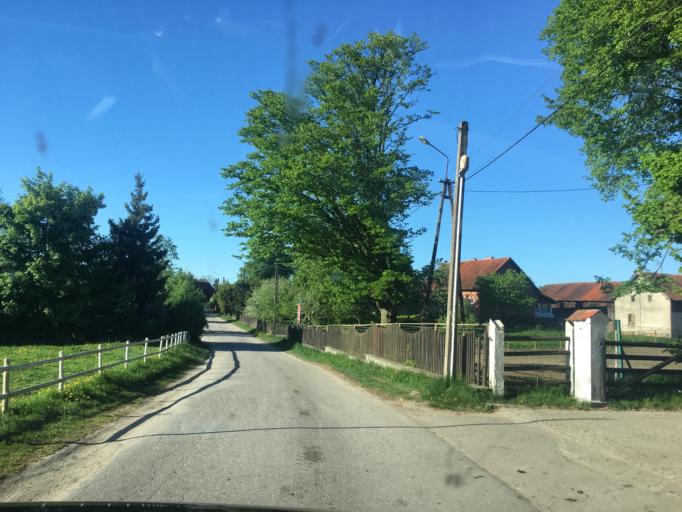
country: PL
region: Warmian-Masurian Voivodeship
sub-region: Powiat piski
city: Ruciane-Nida
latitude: 53.6877
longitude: 21.4692
